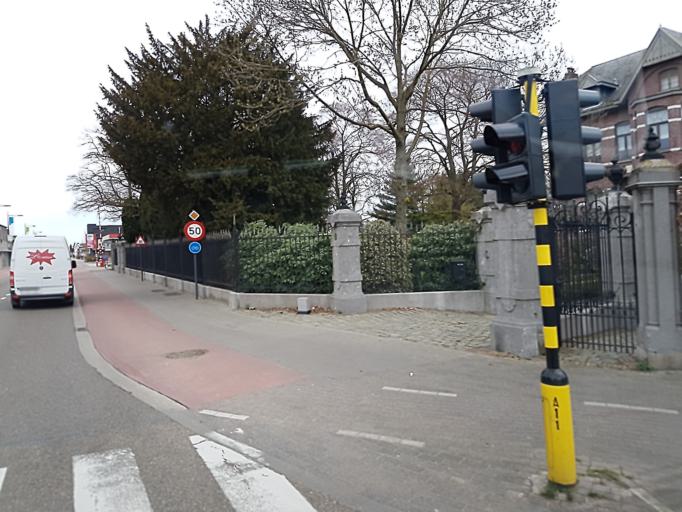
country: BE
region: Flanders
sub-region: Provincie Limburg
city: Overpelt
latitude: 51.2150
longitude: 5.4255
